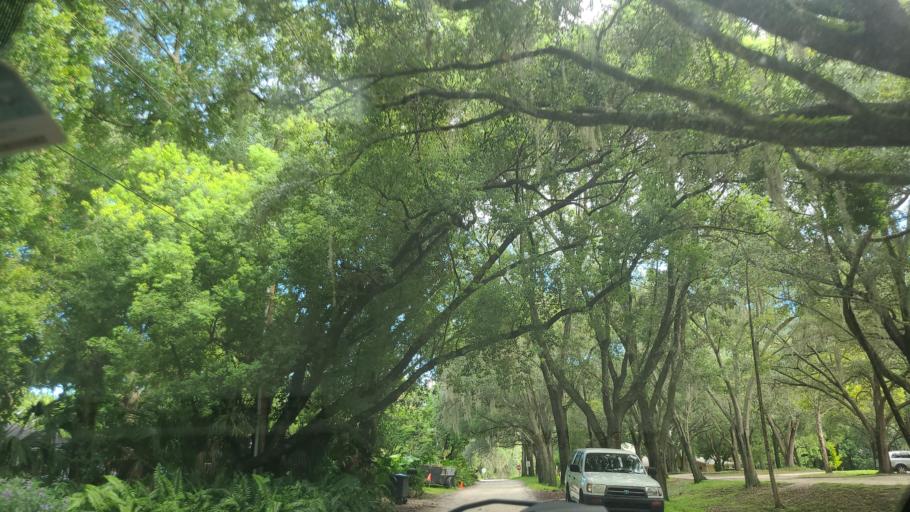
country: US
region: Florida
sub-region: Orange County
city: Windermere
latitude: 28.4966
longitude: -81.5368
